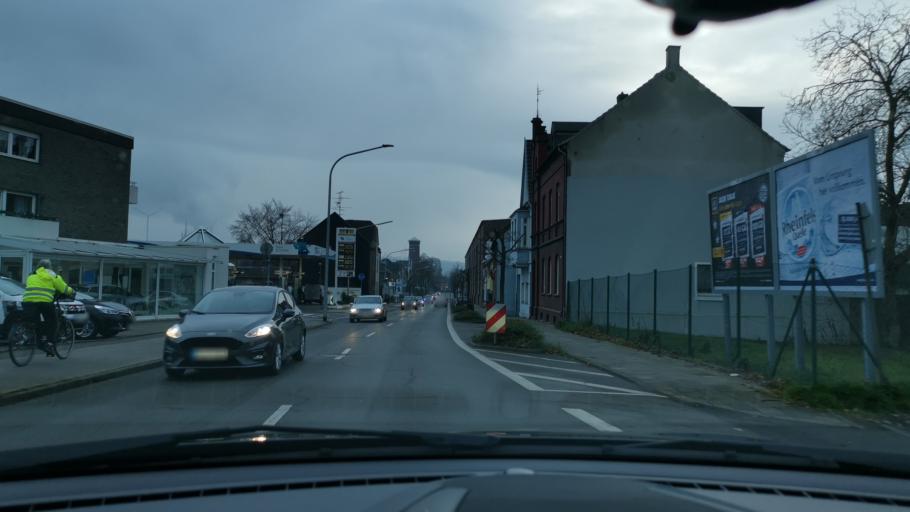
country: DE
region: North Rhine-Westphalia
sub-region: Regierungsbezirk Dusseldorf
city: Grevenbroich
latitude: 51.0913
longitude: 6.6043
